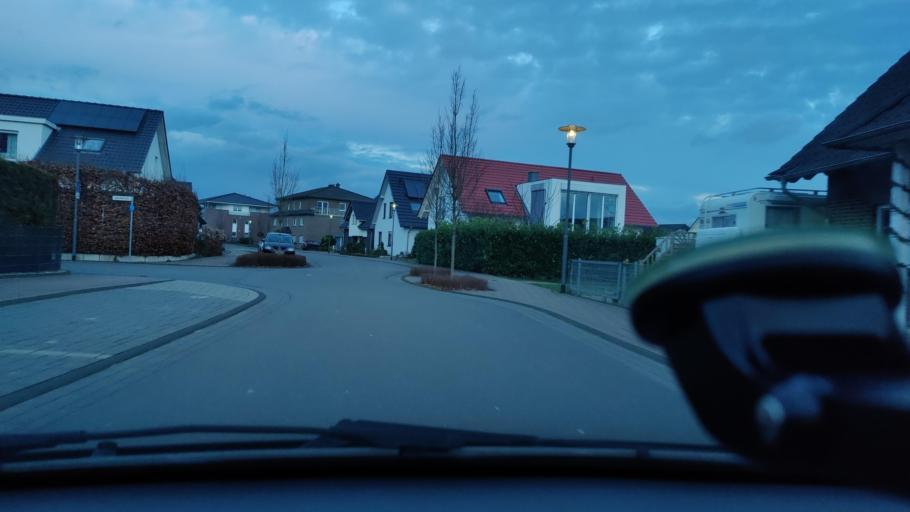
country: DE
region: North Rhine-Westphalia
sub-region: Regierungsbezirk Dusseldorf
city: Xanten
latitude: 51.6649
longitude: 6.4617
